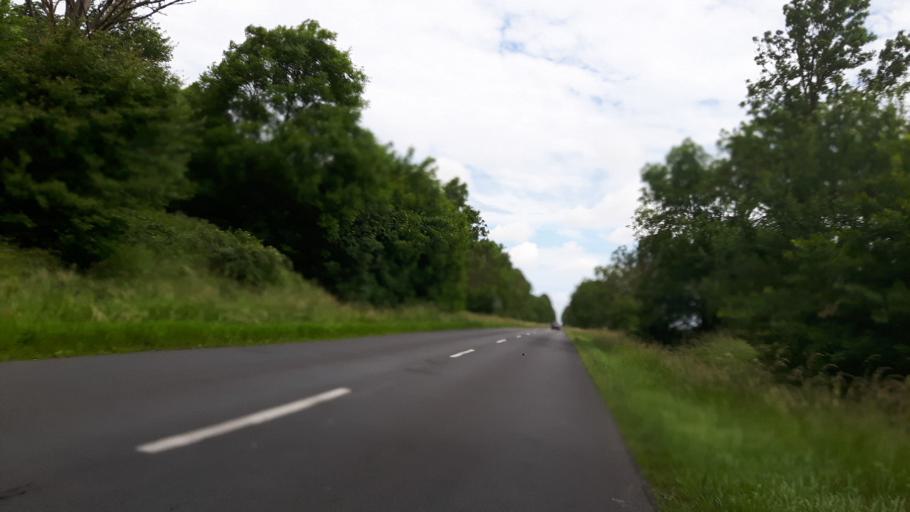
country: PL
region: West Pomeranian Voivodeship
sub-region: Powiat gryficki
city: Trzebiatow
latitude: 54.0314
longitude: 15.2419
